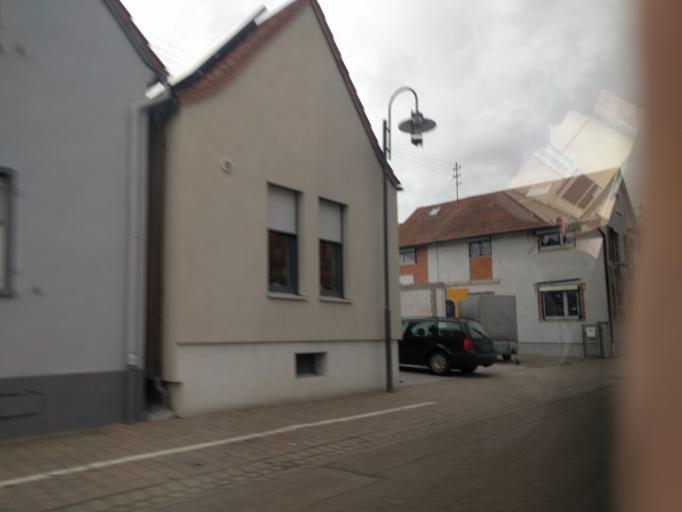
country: DE
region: Rheinland-Pfalz
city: Leimersheim
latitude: 49.1240
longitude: 8.3475
